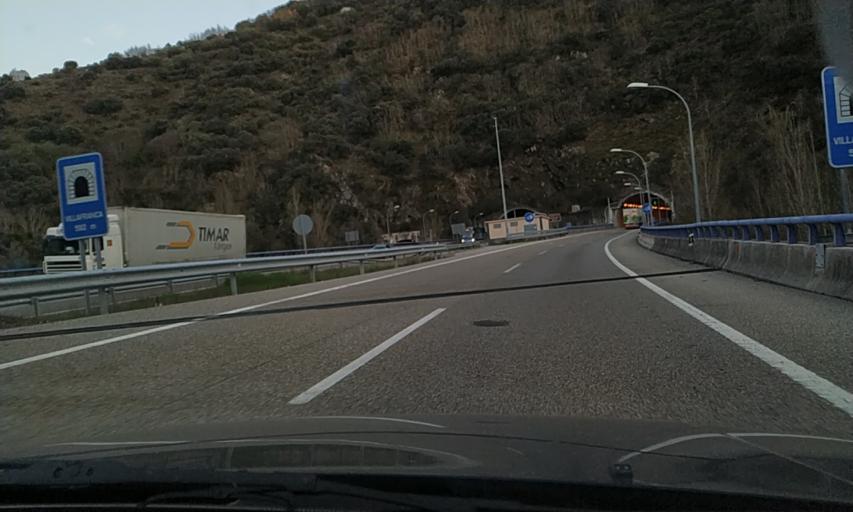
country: ES
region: Castille and Leon
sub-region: Provincia de Leon
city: Villafranca del Bierzo
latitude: 42.6122
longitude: -6.8213
